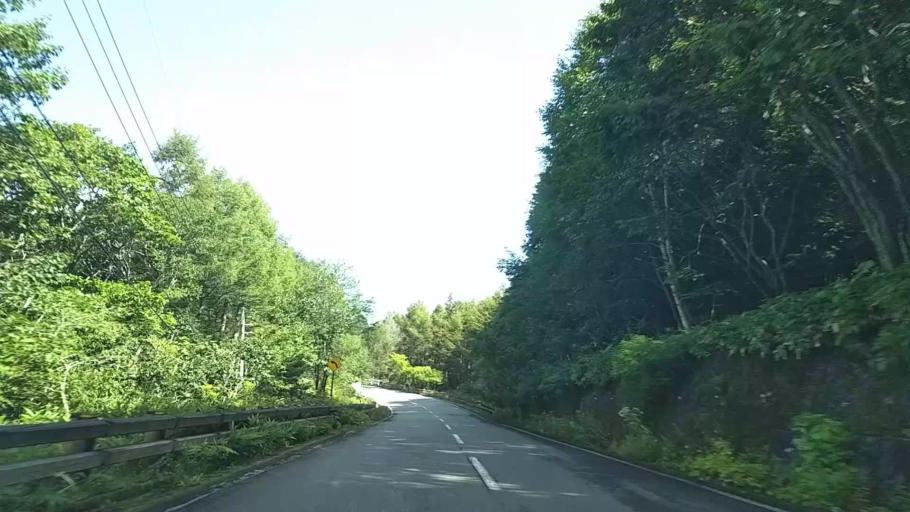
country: JP
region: Nagano
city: Suwa
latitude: 36.1107
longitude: 138.1704
